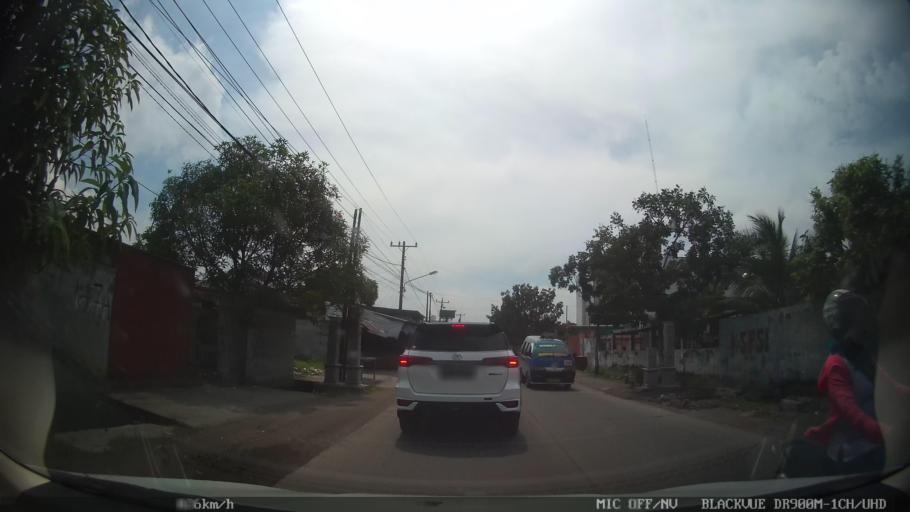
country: ID
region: North Sumatra
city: Labuhan Deli
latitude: 3.6572
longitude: 98.6731
